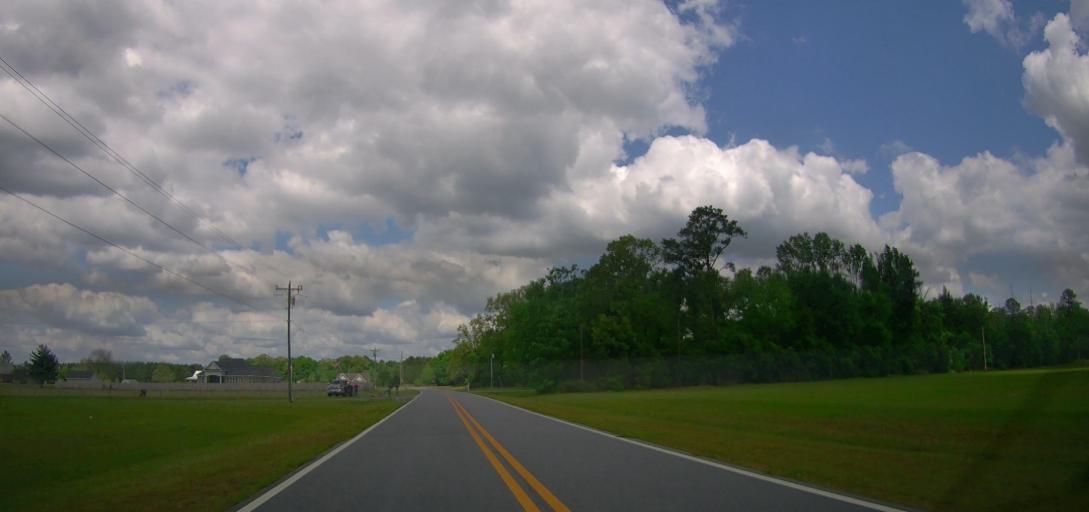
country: US
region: Georgia
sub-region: Laurens County
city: Dublin
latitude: 32.6012
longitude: -82.9374
